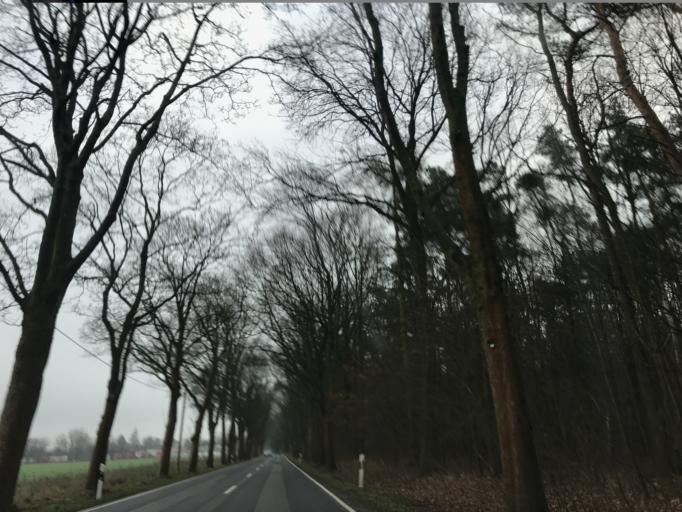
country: DE
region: Brandenburg
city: Kremmen
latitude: 52.7499
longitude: 12.9966
